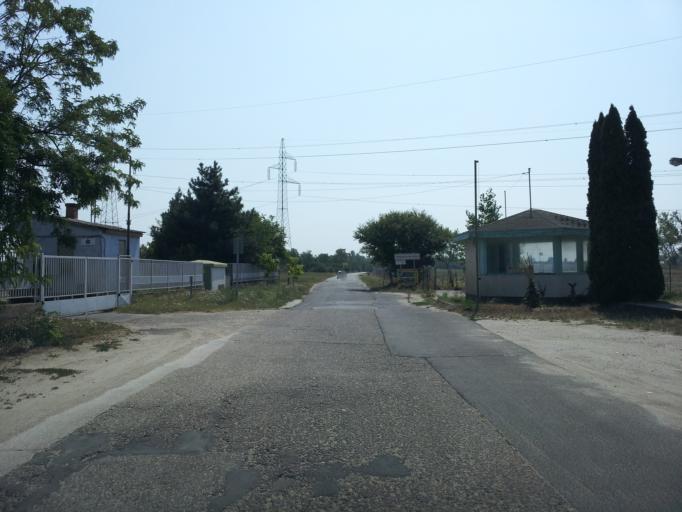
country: HU
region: Pest
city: Dunavarsany
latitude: 47.2702
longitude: 19.0728
